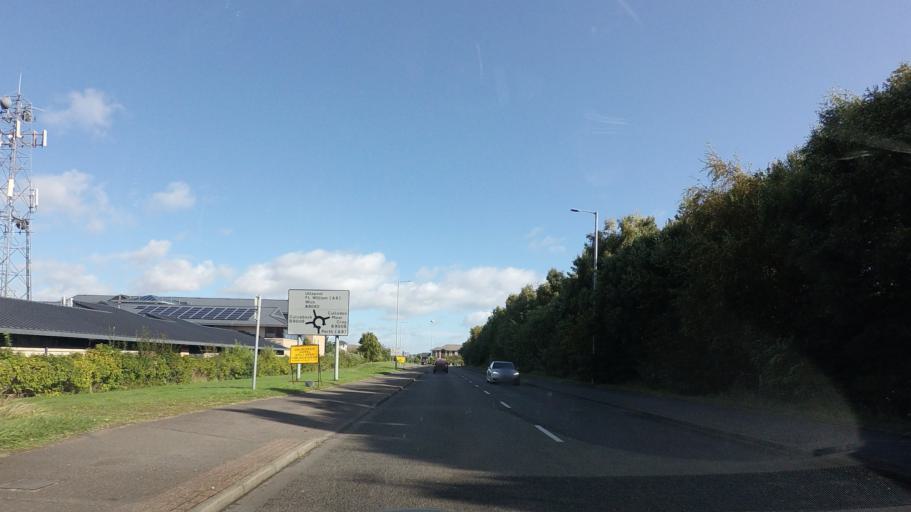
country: GB
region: Scotland
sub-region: Highland
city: Inverness
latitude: 57.4698
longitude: -4.1917
